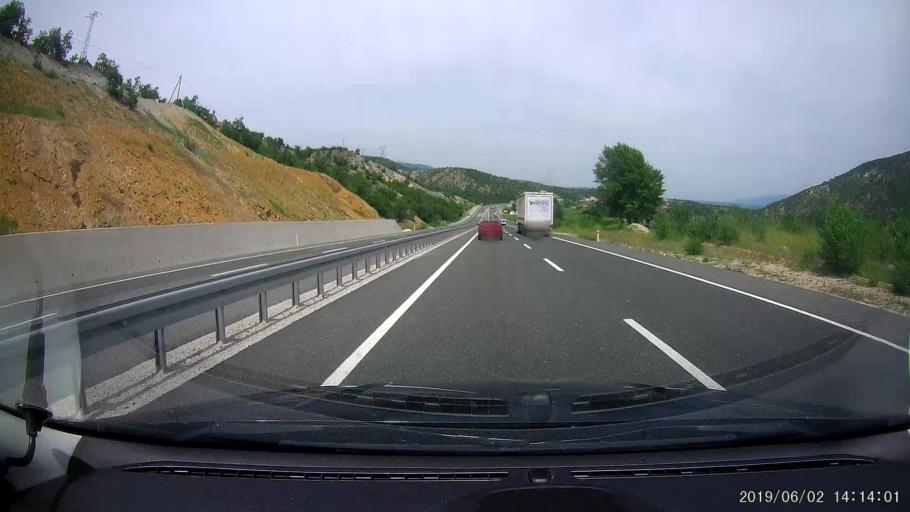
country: TR
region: Cankiri
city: Yaprakli
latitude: 40.9312
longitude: 33.8443
